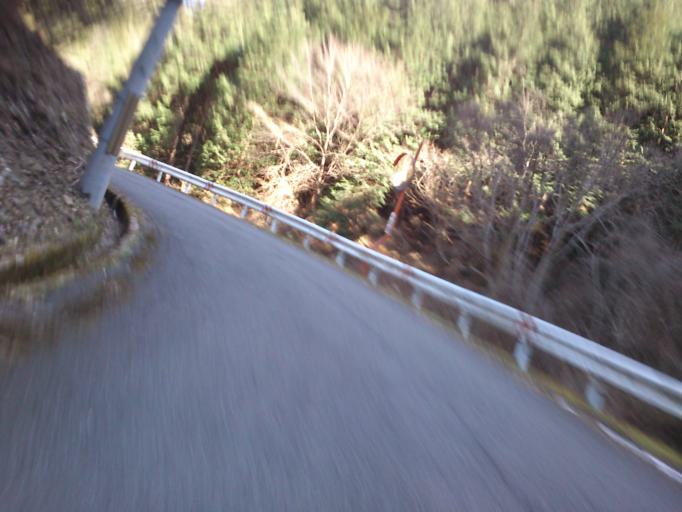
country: JP
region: Kyoto
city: Tanabe
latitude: 34.8104
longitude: 135.8603
